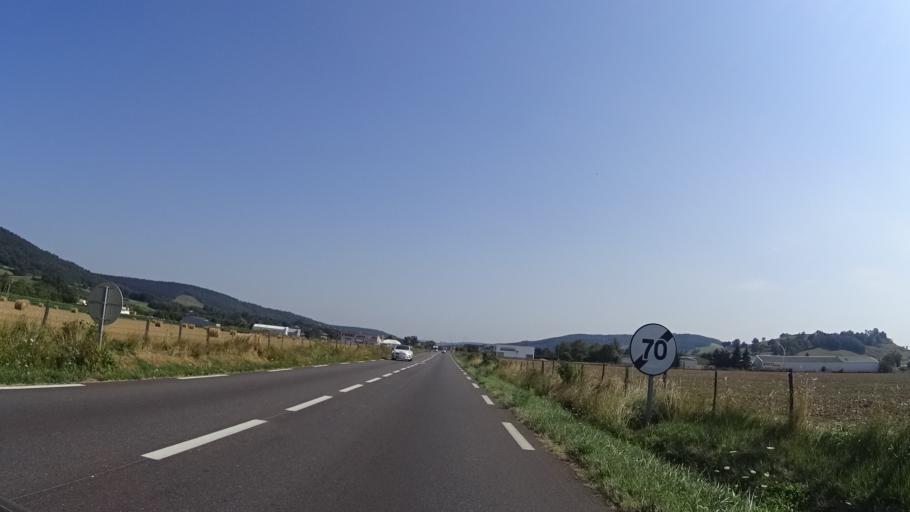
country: FR
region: Midi-Pyrenees
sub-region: Departement de l'Ariege
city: Lavelanet
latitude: 42.9819
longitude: 1.8701
